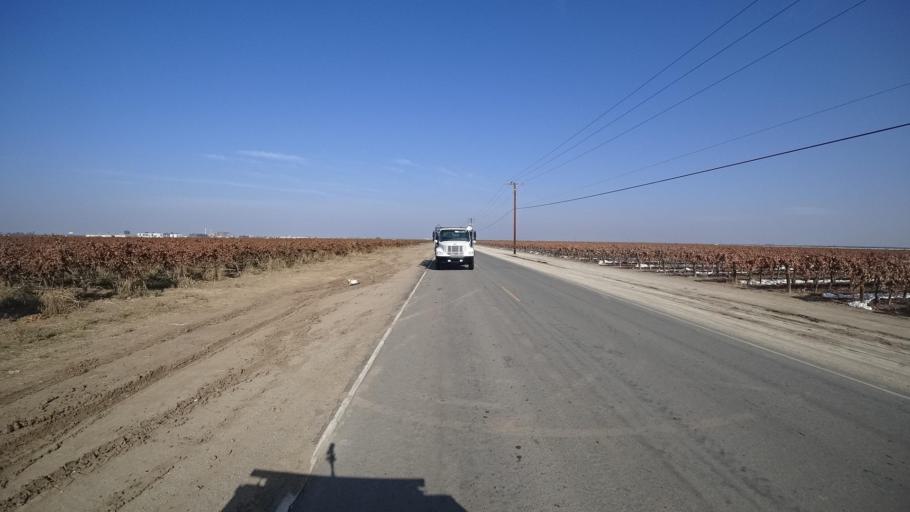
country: US
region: California
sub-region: Kern County
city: McFarland
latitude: 35.7054
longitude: -119.2230
